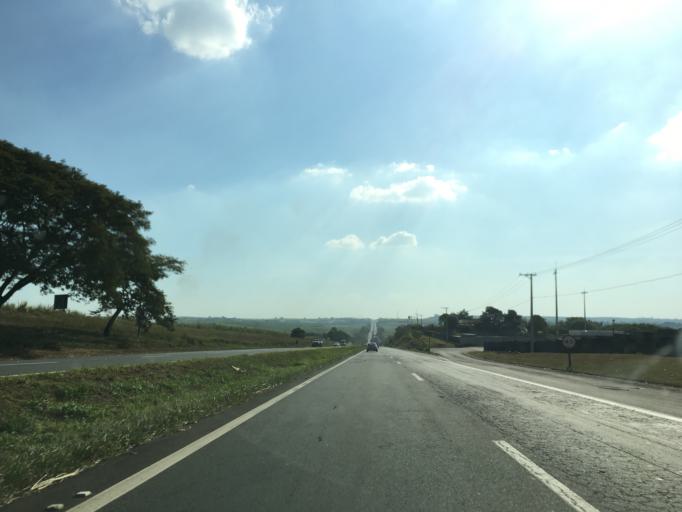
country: BR
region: Sao Paulo
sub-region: Santa Barbara D'Oeste
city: Santa Barbara d'Oeste
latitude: -22.7588
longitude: -47.4680
